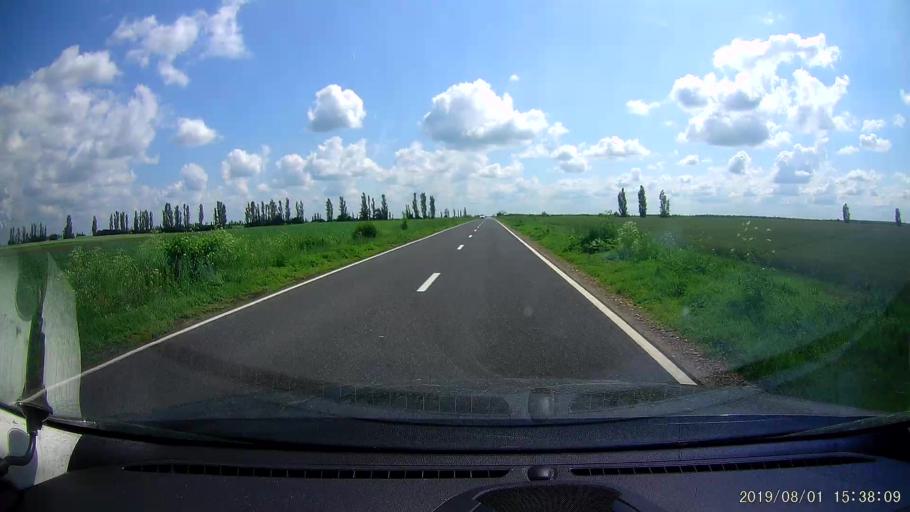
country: RO
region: Braila
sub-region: Comuna Insuratei
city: Insuratei
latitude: 44.8884
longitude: 27.5802
